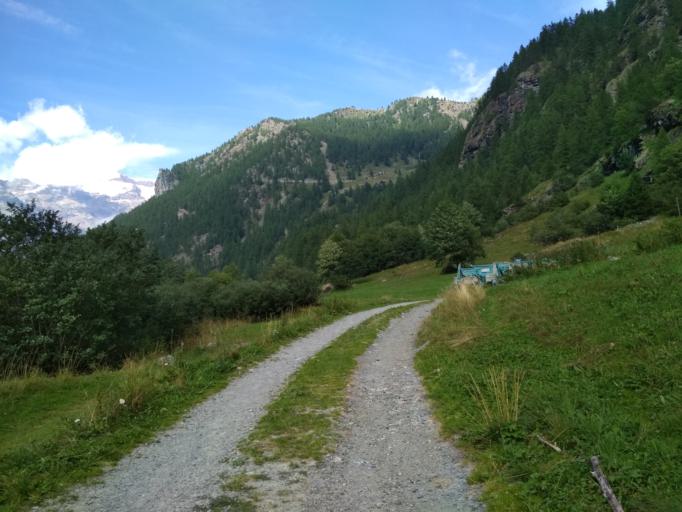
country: IT
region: Aosta Valley
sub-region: Valle d'Aosta
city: Gressoney-La-Trinite
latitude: 45.8239
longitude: 7.8264
